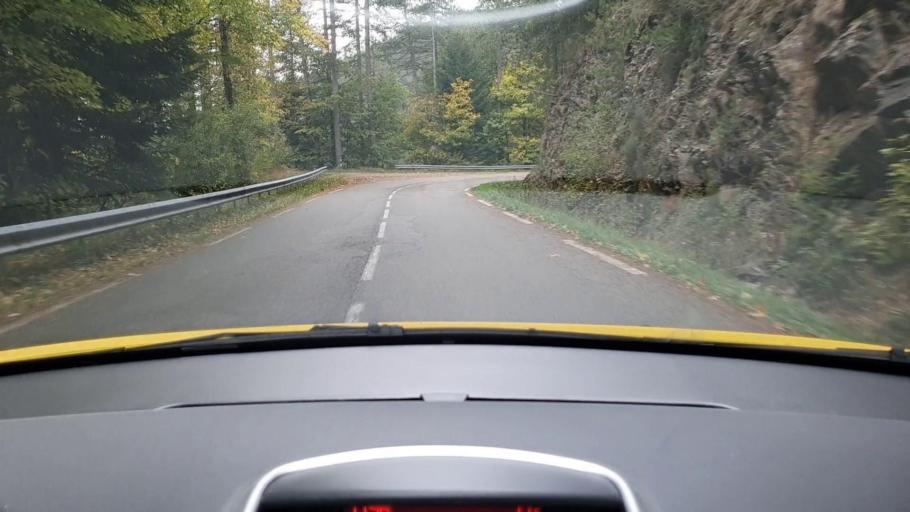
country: FR
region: Languedoc-Roussillon
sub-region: Departement de la Lozere
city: Meyrueis
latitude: 44.1320
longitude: 3.4300
